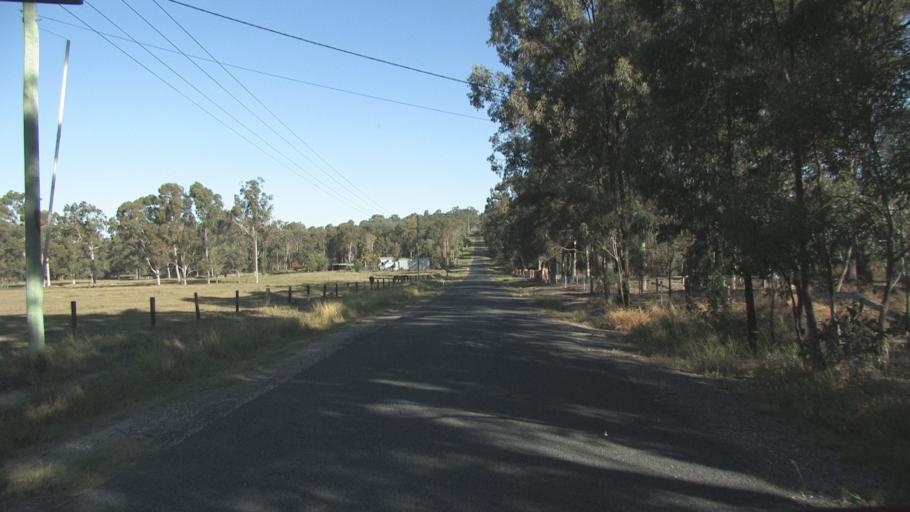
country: AU
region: Queensland
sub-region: Logan
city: Logan Reserve
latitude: -27.7187
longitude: 153.1066
